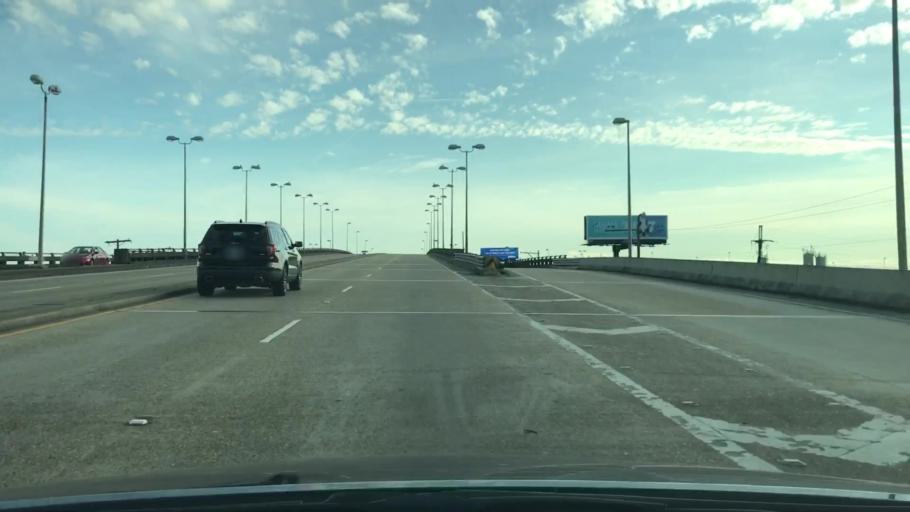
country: US
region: Louisiana
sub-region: Jefferson Parish
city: Metairie
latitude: 29.9772
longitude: -90.1563
